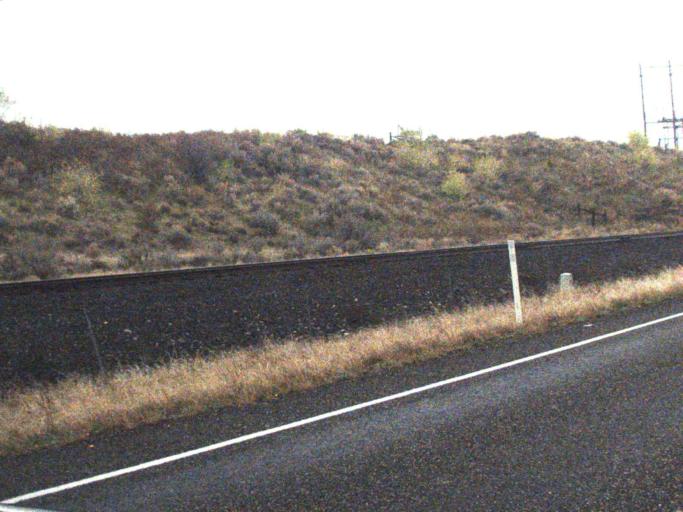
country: US
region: Washington
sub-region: Asotin County
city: Clarkston Heights-Vineland
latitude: 46.4244
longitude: -117.0978
